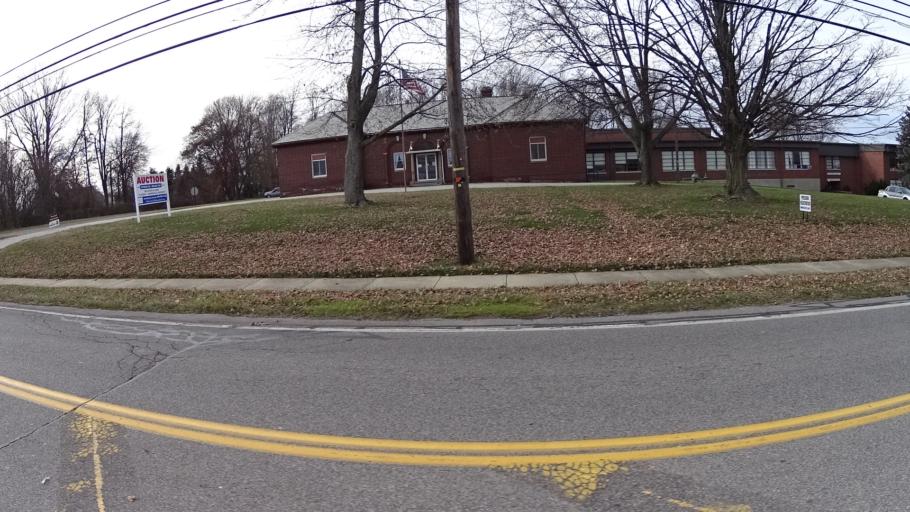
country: US
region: Ohio
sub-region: Lorain County
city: North Ridgeville
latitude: 41.3690
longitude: -81.9981
